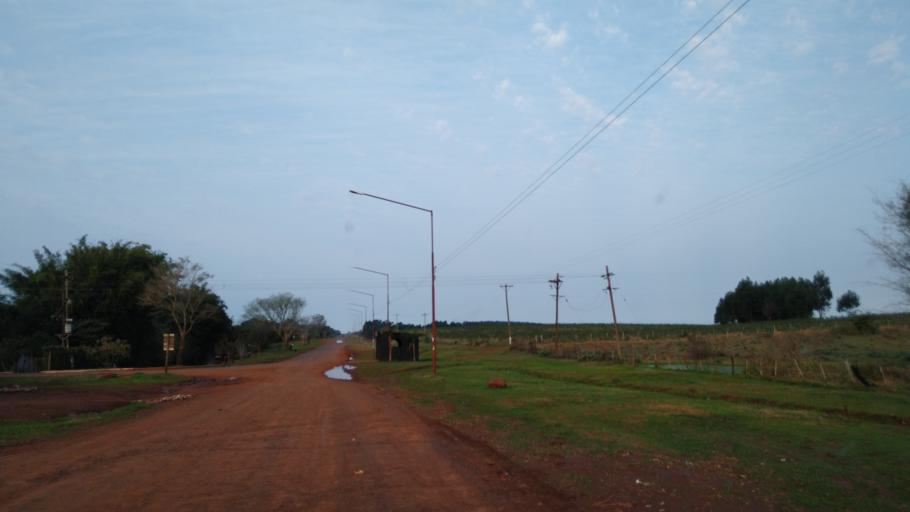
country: AR
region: Corrientes
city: San Carlos
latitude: -27.7520
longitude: -55.8987
